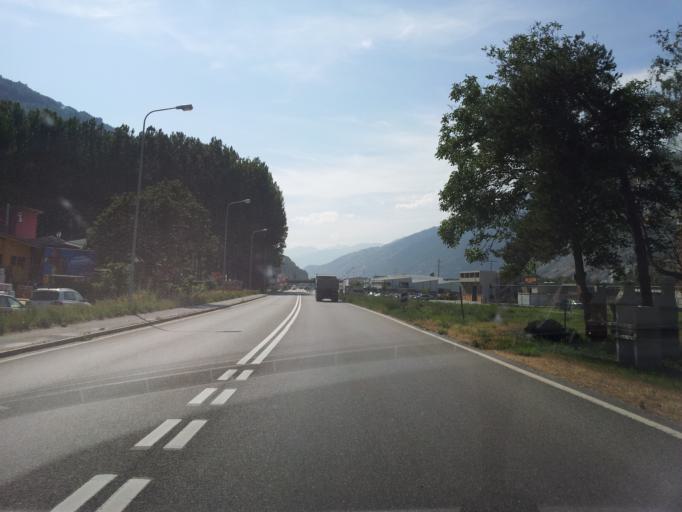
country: CH
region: Valais
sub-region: Raron District
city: Raron
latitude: 46.3040
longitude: 7.7982
